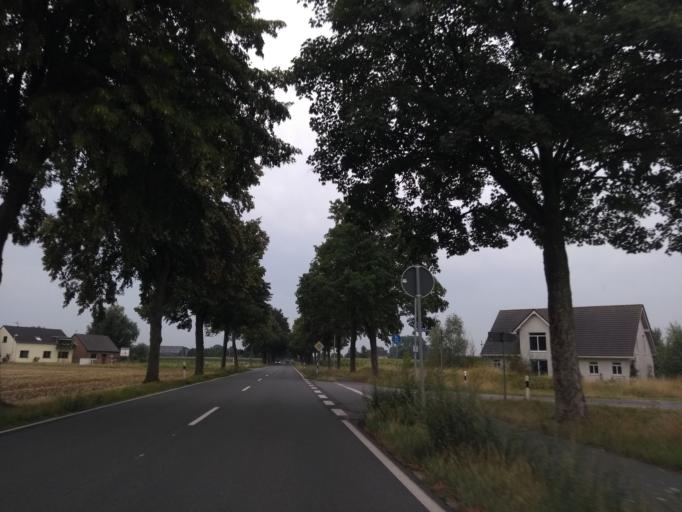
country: DE
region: North Rhine-Westphalia
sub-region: Regierungsbezirk Dusseldorf
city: Kleve
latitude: 51.8437
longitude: 6.0845
